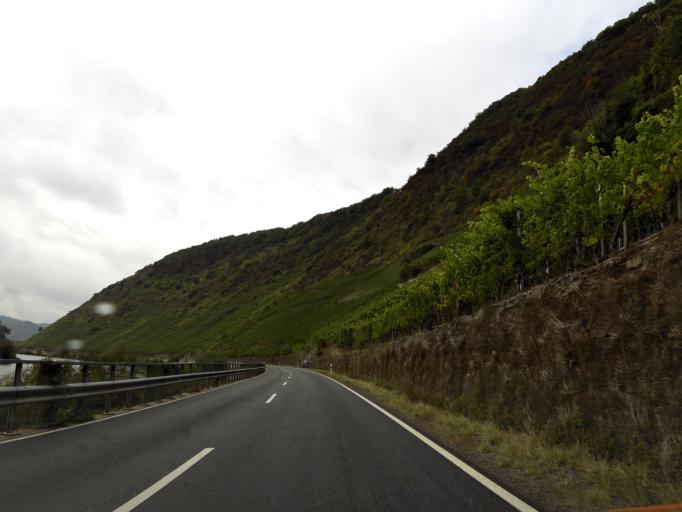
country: DE
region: Rheinland-Pfalz
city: Ernst
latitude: 50.1468
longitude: 7.2298
